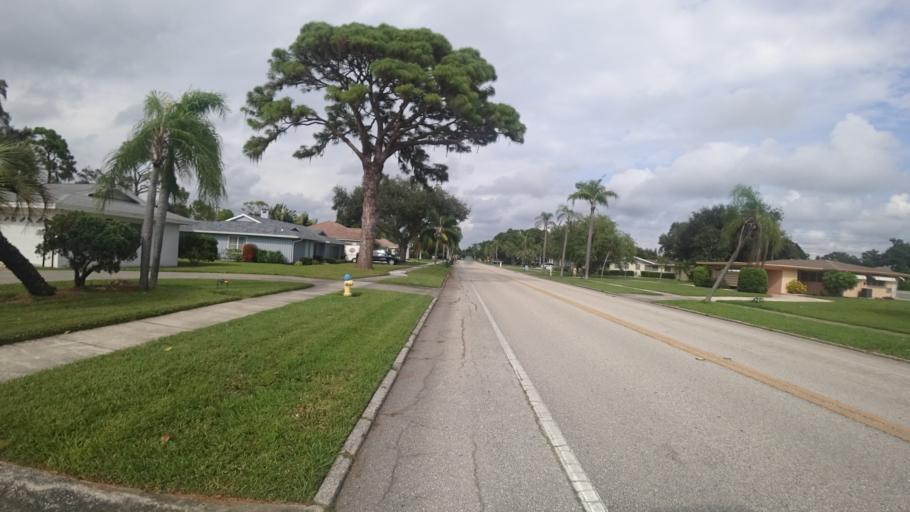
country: US
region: Florida
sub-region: Manatee County
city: Whitfield
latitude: 27.4160
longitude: -82.5612
